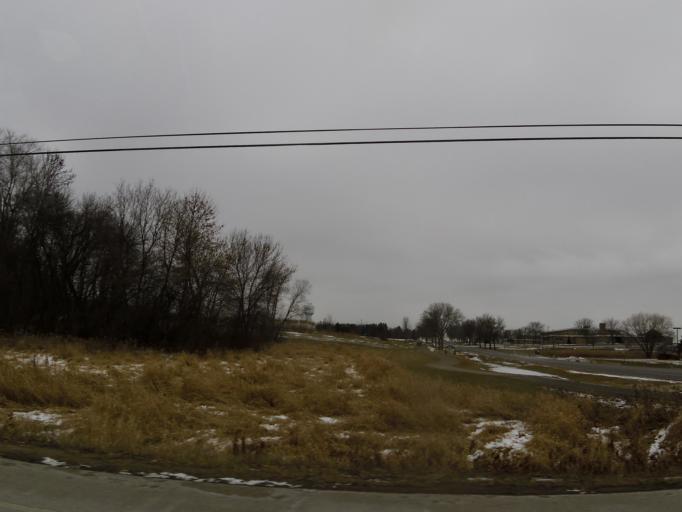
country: US
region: Minnesota
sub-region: Hennepin County
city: Long Lake
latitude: 44.9982
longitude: -93.5941
